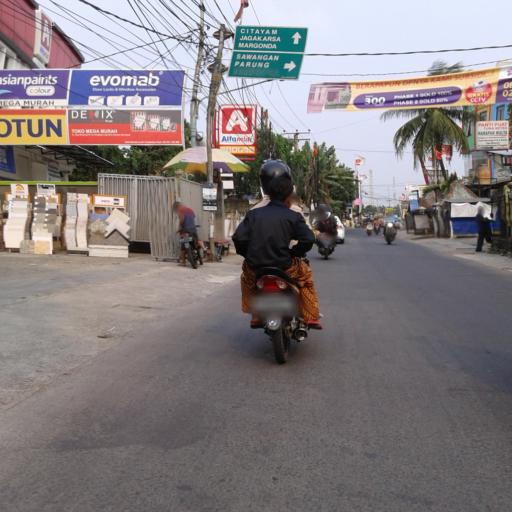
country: ID
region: West Java
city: Sawangan
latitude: -6.3942
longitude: 106.7718
